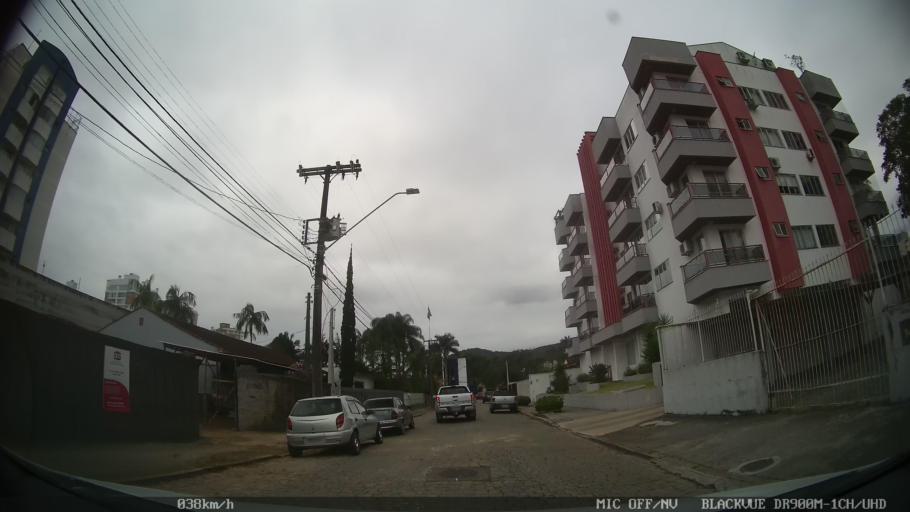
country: BR
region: Santa Catarina
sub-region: Joinville
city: Joinville
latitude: -26.2843
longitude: -48.8459
